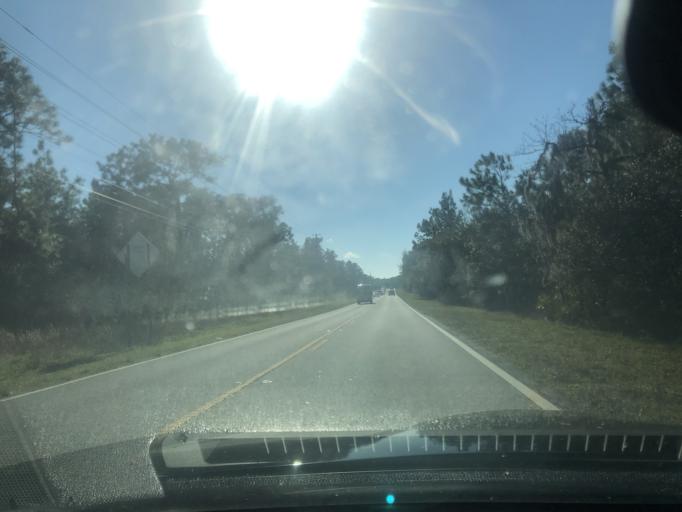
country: US
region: Florida
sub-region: Citrus County
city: Lecanto
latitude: 28.8236
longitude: -82.5287
